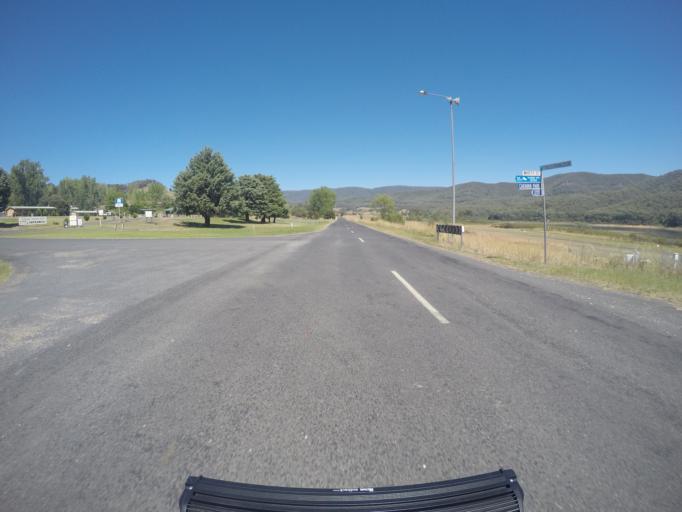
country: AU
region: New South Wales
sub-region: Tumut Shire
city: Tumut
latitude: -35.5828
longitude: 148.2939
